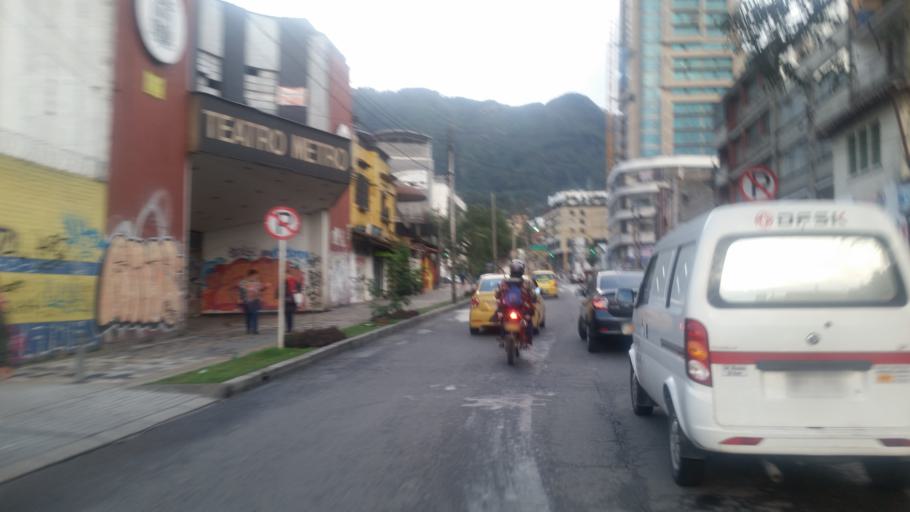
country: CO
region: Bogota D.C.
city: Bogota
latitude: 4.6223
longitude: -74.0687
